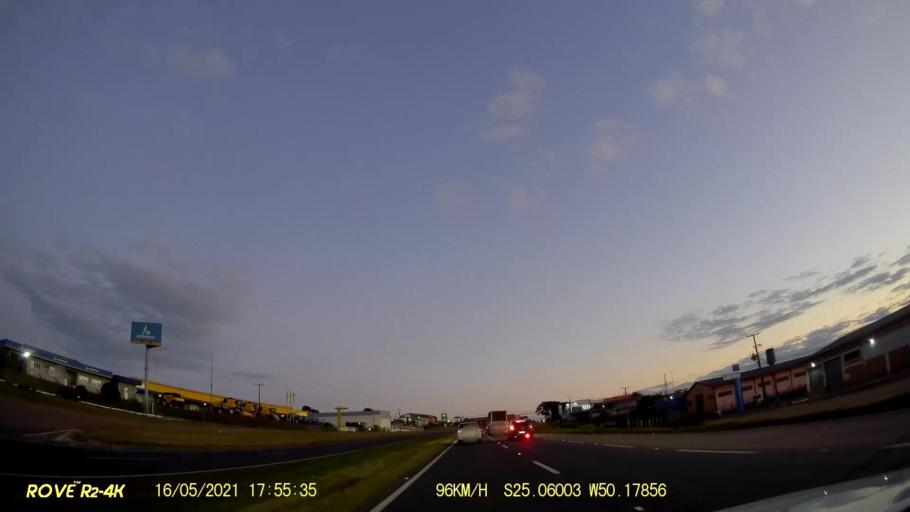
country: BR
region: Parana
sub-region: Ponta Grossa
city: Ponta Grossa
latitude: -25.0601
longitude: -50.1785
